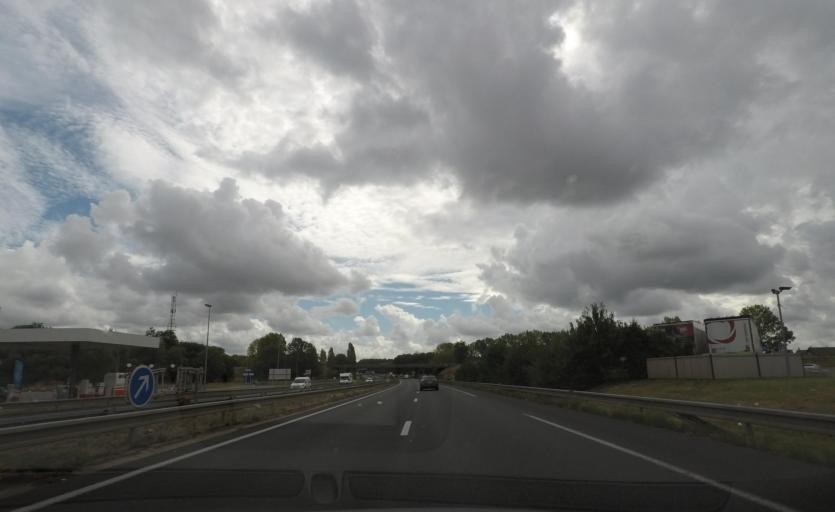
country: FR
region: Pays de la Loire
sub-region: Departement de Maine-et-Loire
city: Ecouflant
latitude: 47.5008
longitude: -0.4901
